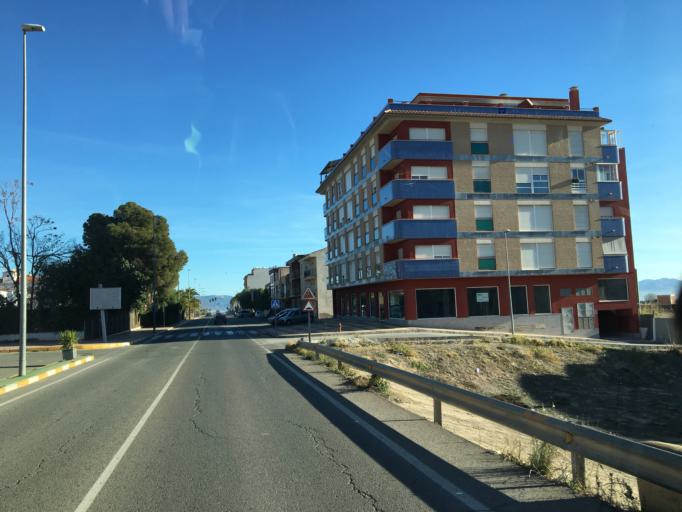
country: ES
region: Murcia
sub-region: Murcia
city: Puerto Lumbreras
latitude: 37.5698
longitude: -1.8009
